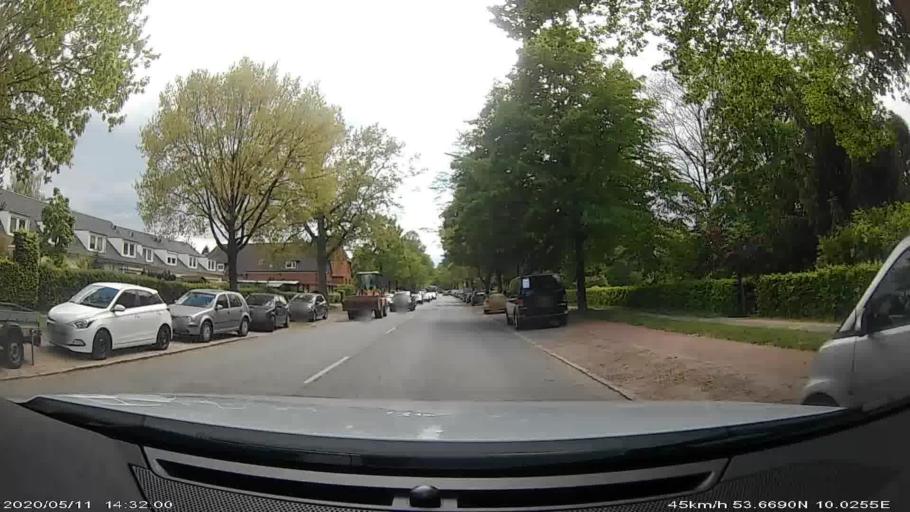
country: DE
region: Hamburg
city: Langenhorn
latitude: 53.6591
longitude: 10.0206
